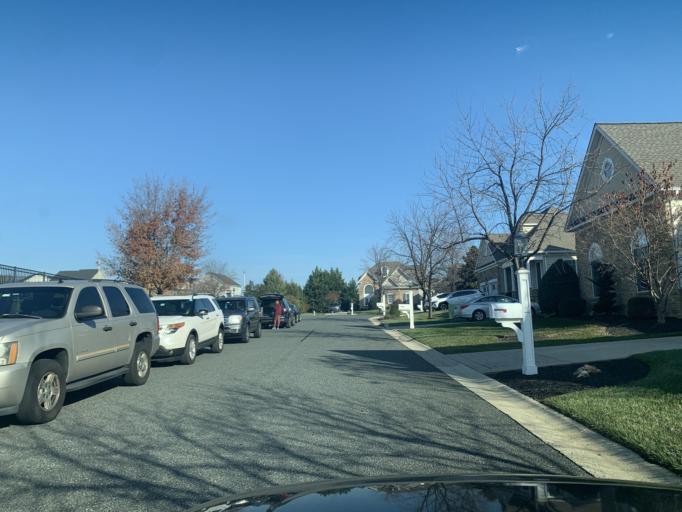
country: US
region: Maryland
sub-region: Harford County
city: Havre de Grace
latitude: 39.5534
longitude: -76.1268
